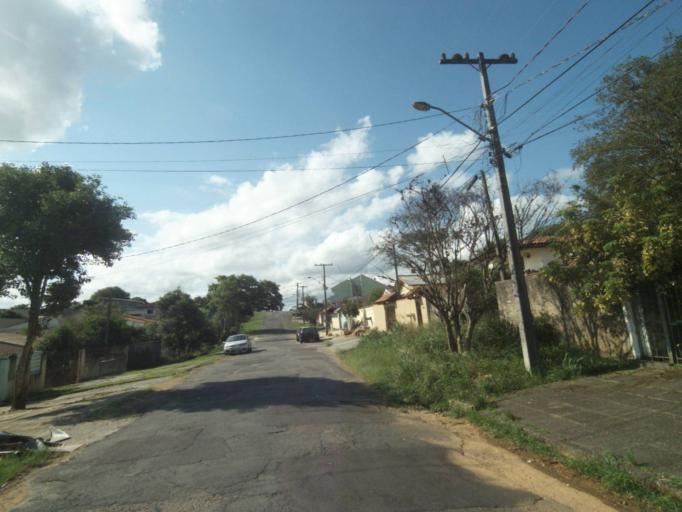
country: BR
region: Parana
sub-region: Curitiba
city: Curitiba
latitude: -25.3913
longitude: -49.3006
